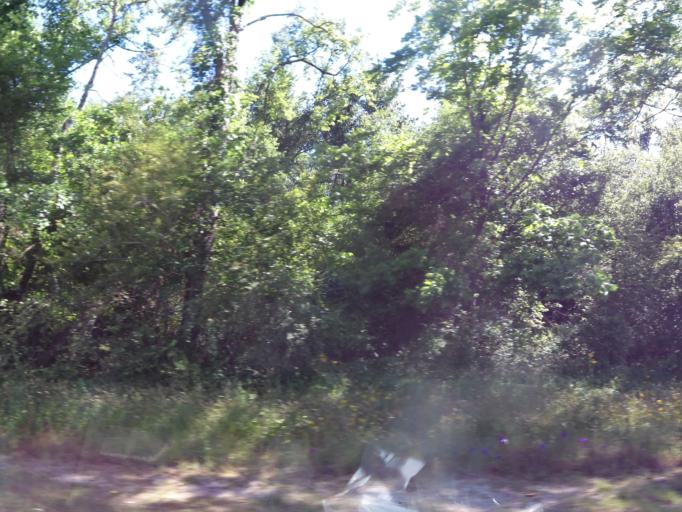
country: US
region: South Carolina
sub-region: Bamberg County
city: Denmark
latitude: 33.3413
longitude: -81.1827
